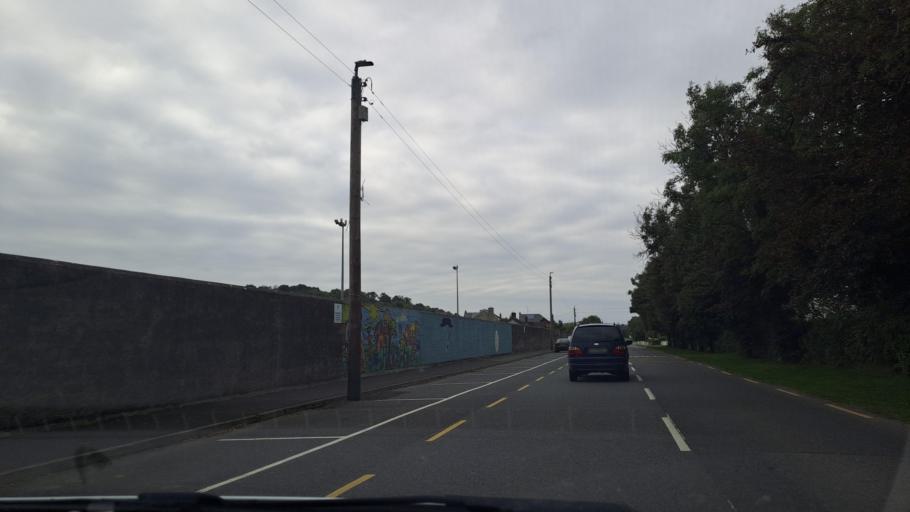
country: IE
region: Ulster
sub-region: County Monaghan
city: Carrickmacross
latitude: 53.9854
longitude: -6.7204
